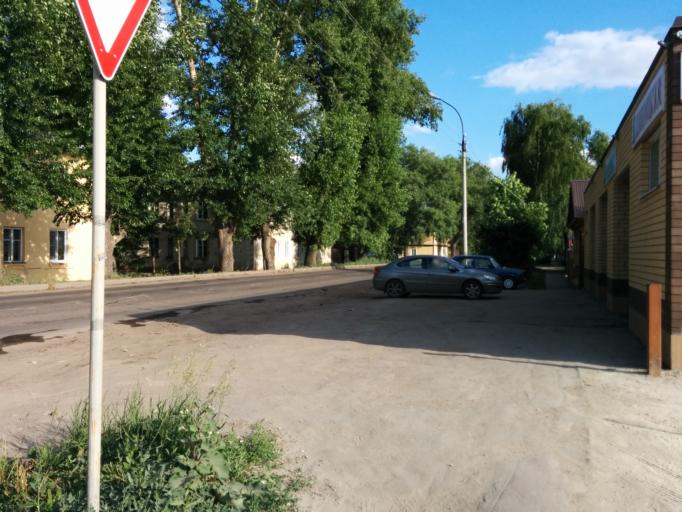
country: RU
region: Tambov
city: Tambov
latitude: 52.7520
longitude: 41.4401
